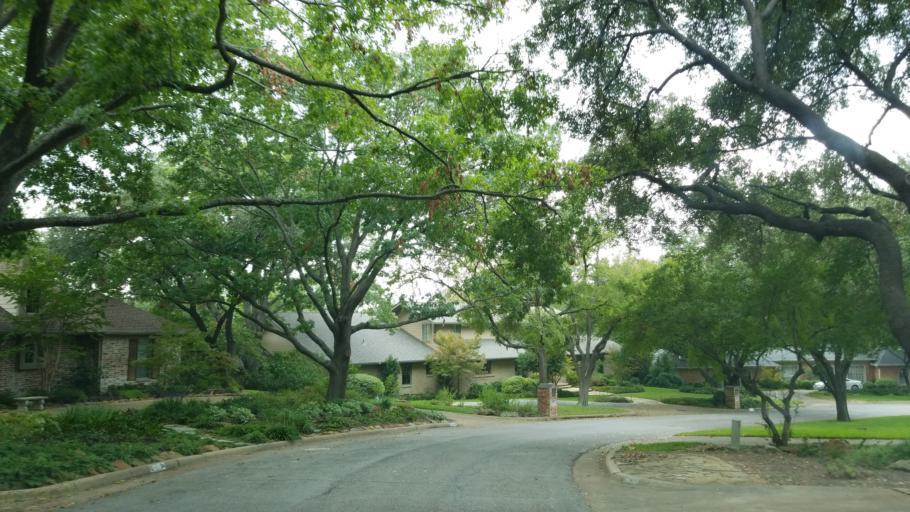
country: US
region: Texas
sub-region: Dallas County
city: Addison
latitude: 32.9477
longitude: -96.7869
